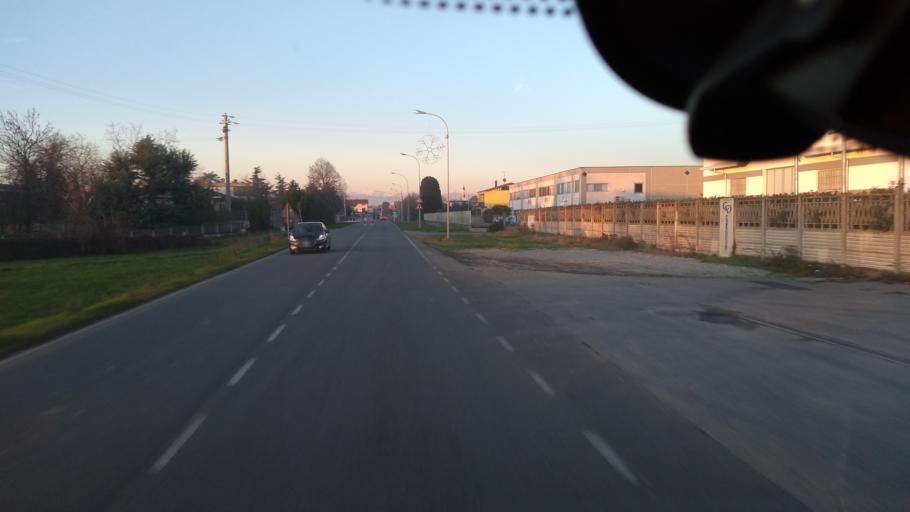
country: IT
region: Lombardy
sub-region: Provincia di Bergamo
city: Calvenzano
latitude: 45.4865
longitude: 9.6011
